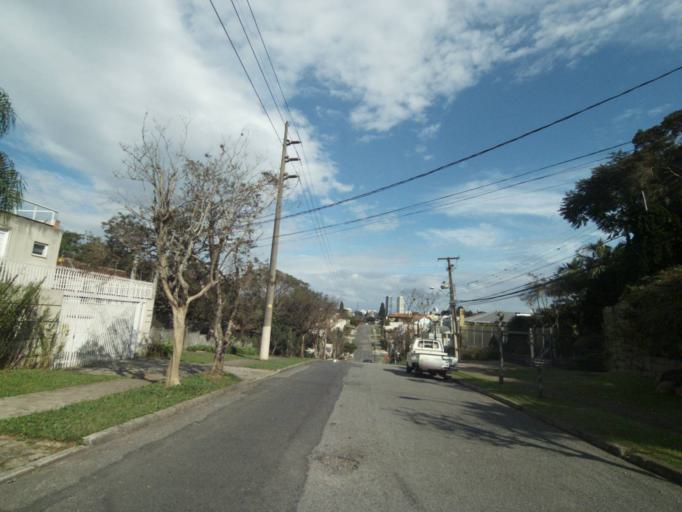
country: BR
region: Parana
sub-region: Curitiba
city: Curitiba
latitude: -25.4117
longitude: -49.2822
